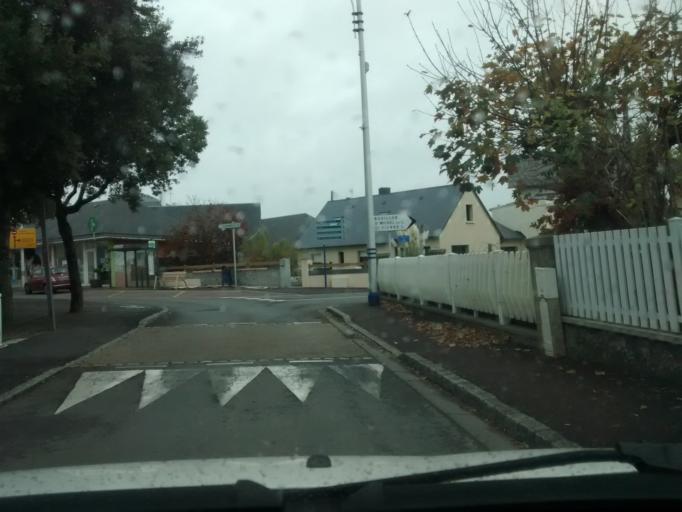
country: FR
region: Lower Normandy
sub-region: Departement de la Manche
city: Jullouville
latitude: 48.7742
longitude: -1.5672
